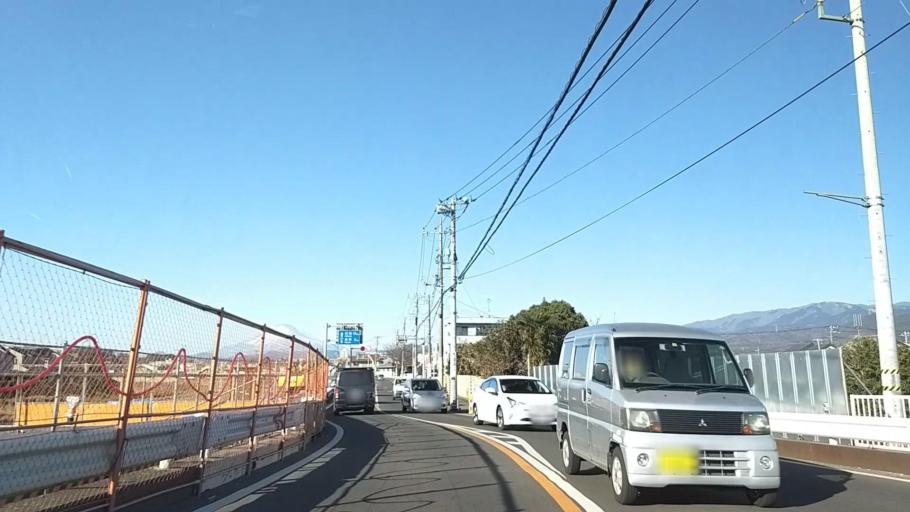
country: JP
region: Kanagawa
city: Isehara
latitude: 35.3596
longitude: 139.2979
